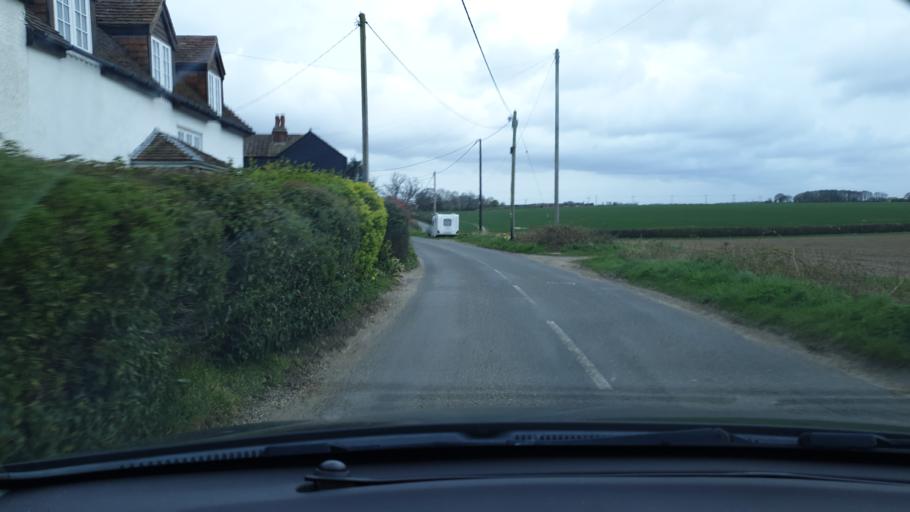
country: GB
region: England
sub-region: Essex
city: Mistley
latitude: 51.9358
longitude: 1.1746
